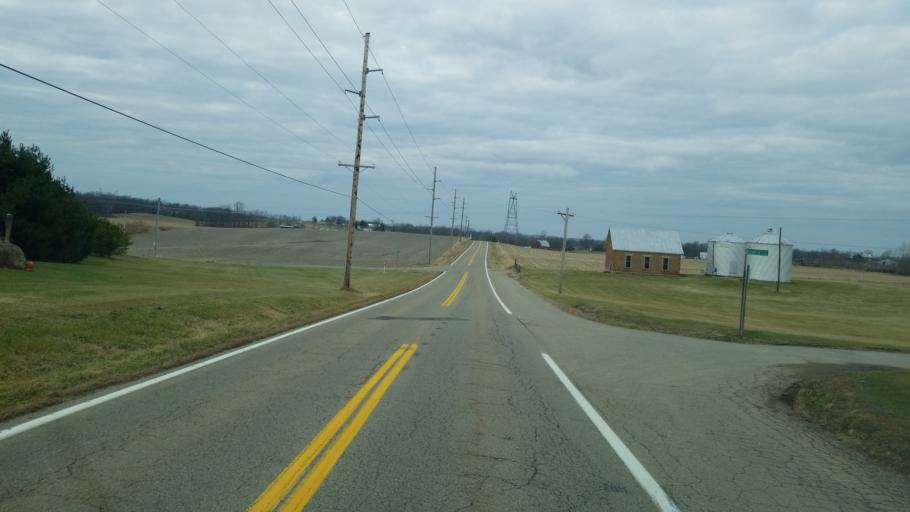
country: US
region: Ohio
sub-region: Ross County
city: Frankfort
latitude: 39.3558
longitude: -83.2669
